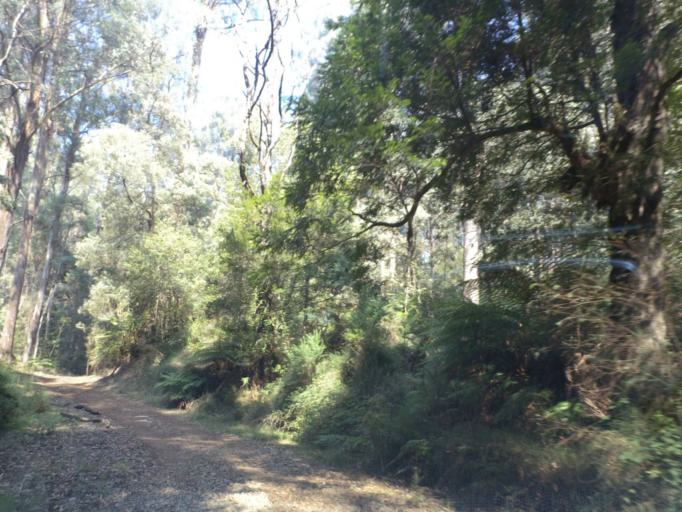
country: AU
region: Victoria
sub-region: Yarra Ranges
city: Healesville
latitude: -37.5661
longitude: 145.6141
